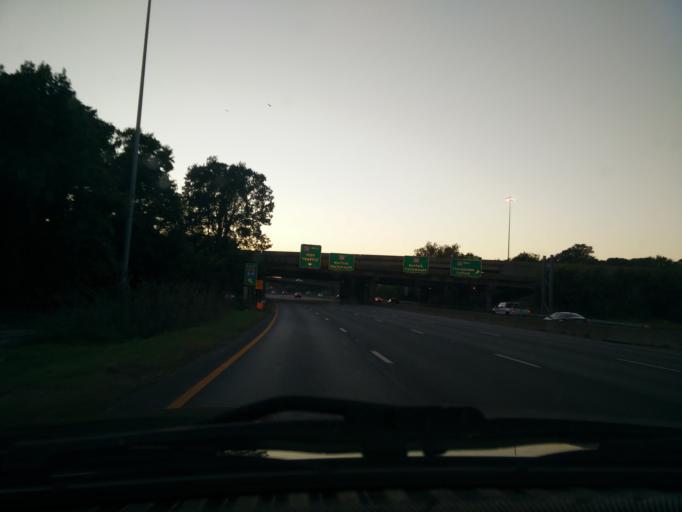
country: US
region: Virginia
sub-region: City of Chesapeake
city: Chesapeake
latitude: 36.8460
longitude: -76.1950
